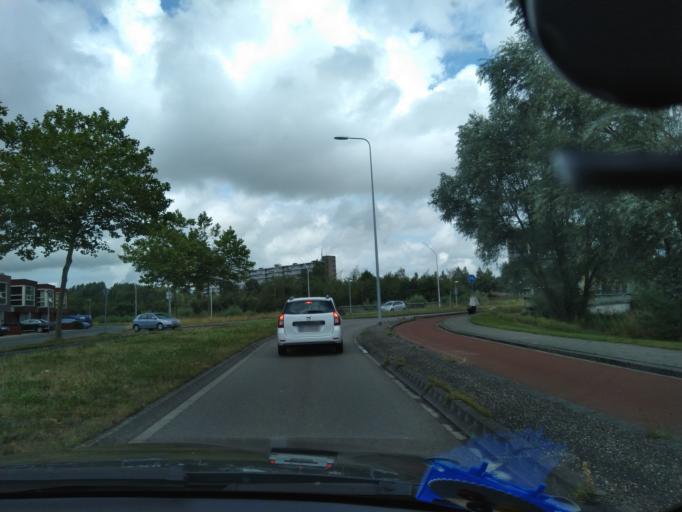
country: NL
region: Groningen
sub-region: Gemeente Groningen
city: Groningen
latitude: 53.2239
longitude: 6.5199
